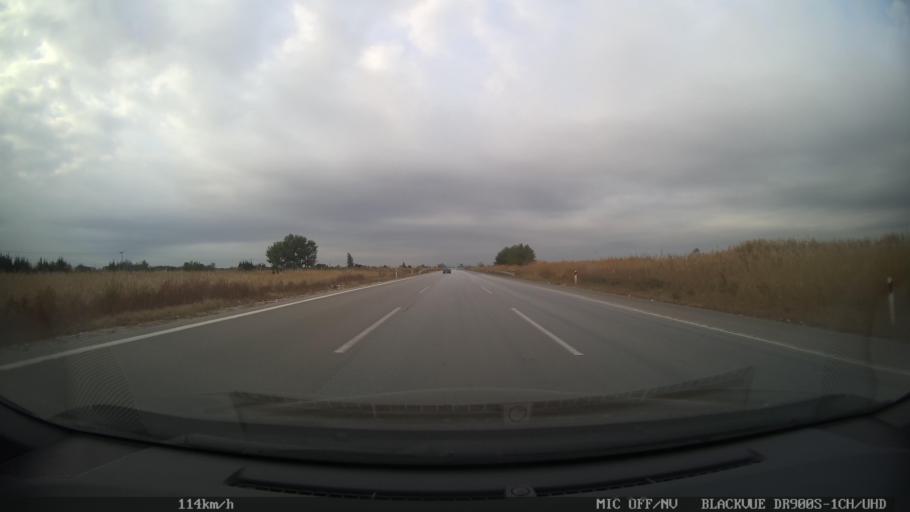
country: GR
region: Central Macedonia
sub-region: Nomos Thessalonikis
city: Chalastra
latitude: 40.6252
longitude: 22.7644
